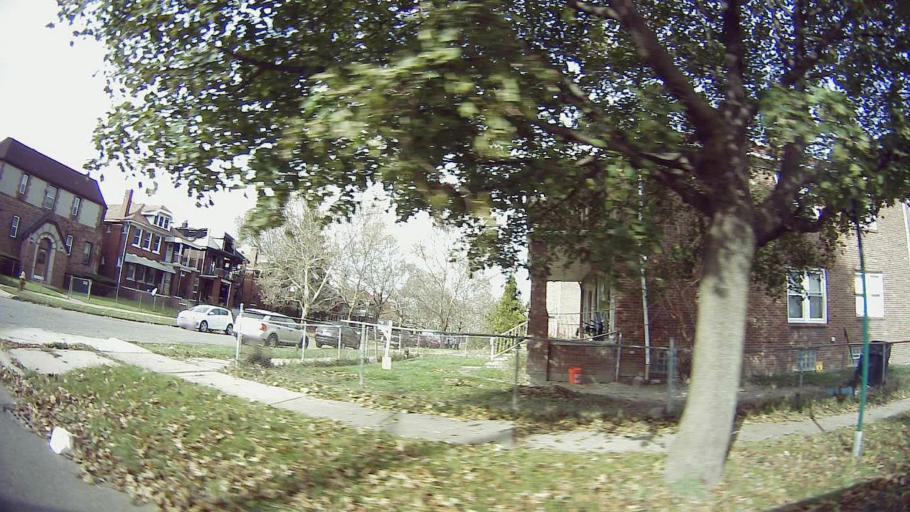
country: US
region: Michigan
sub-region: Wayne County
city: Highland Park
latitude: 42.3761
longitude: -83.1433
